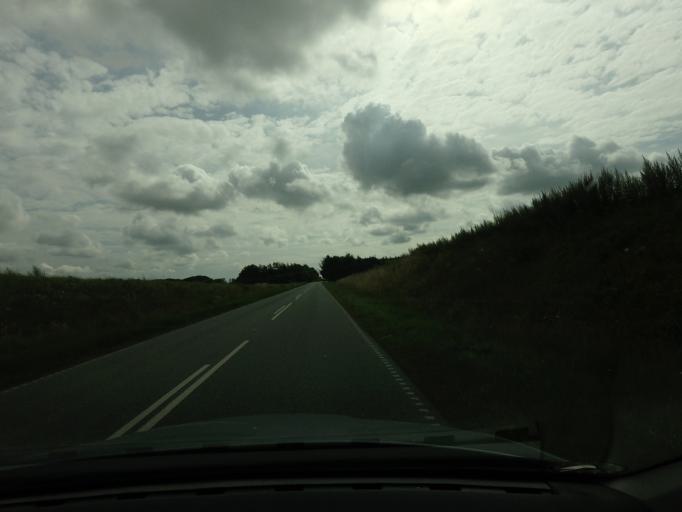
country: DK
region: North Denmark
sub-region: Bronderslev Kommune
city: Dronninglund
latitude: 57.2856
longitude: 10.3280
